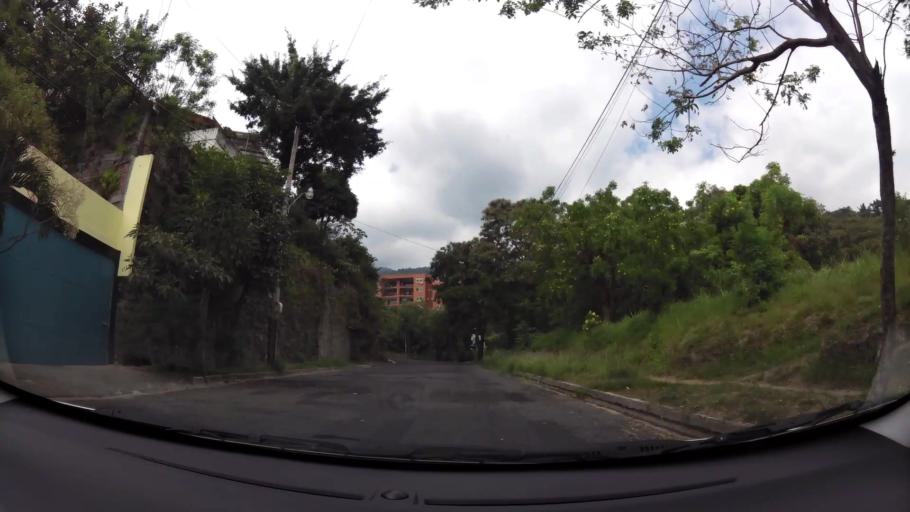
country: SV
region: La Libertad
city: Santa Tecla
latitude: 13.7082
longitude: -89.2575
